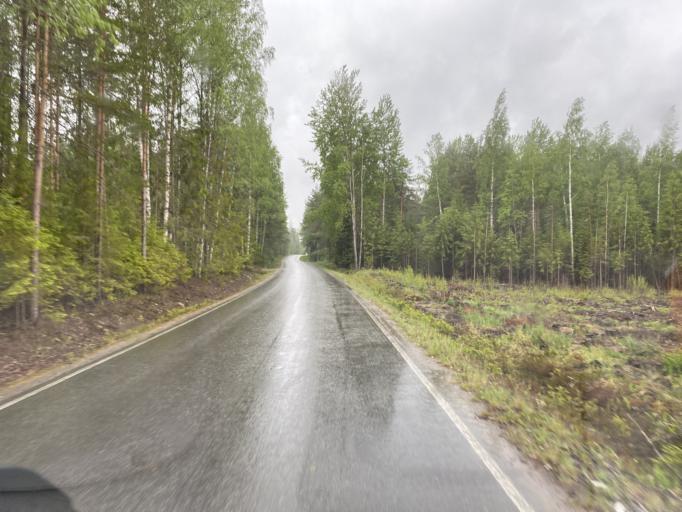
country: FI
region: Haeme
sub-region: Forssa
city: Humppila
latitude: 61.0855
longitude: 23.3098
